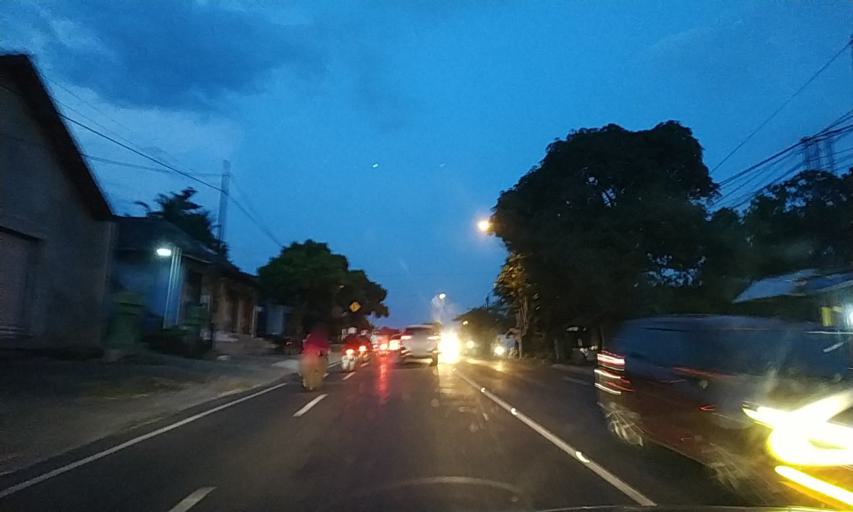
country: ID
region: Daerah Istimewa Yogyakarta
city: Godean
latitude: -7.8132
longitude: 110.2633
